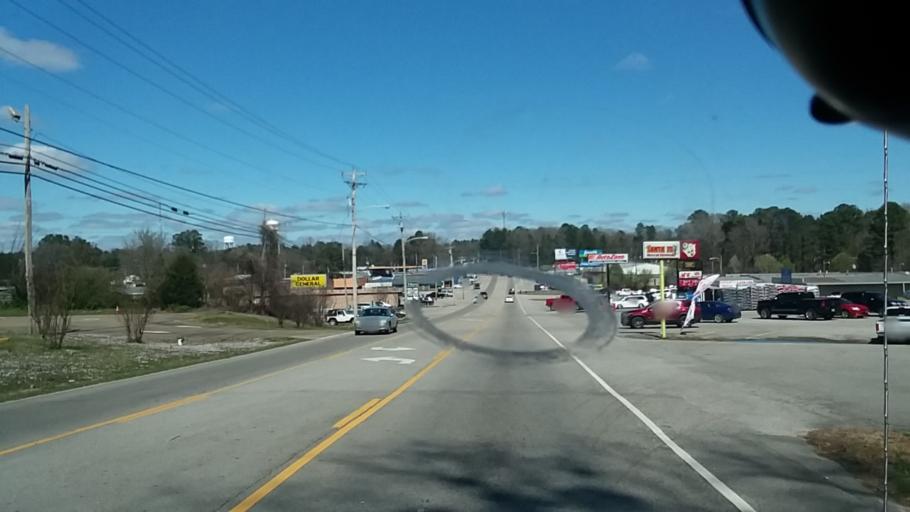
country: US
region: Mississippi
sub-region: Tishomingo County
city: Iuka
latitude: 34.8072
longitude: -88.2008
